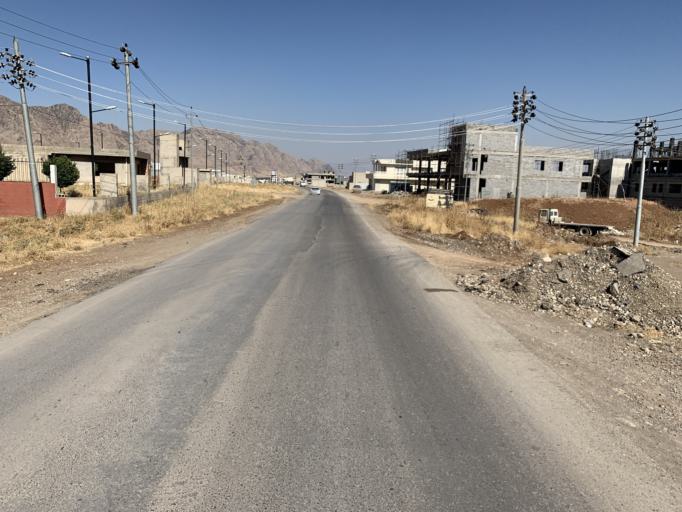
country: IQ
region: As Sulaymaniyah
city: Raniye
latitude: 36.2611
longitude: 44.8555
